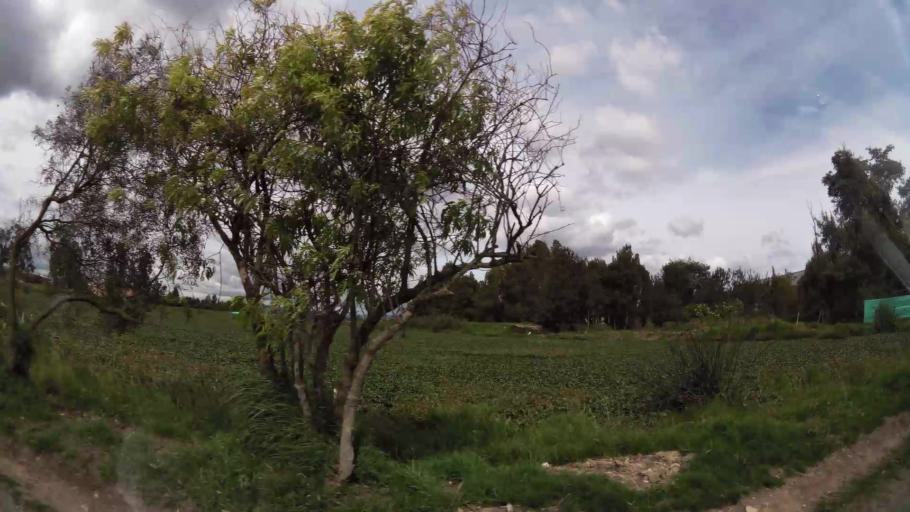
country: CO
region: Cundinamarca
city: Funza
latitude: 4.7012
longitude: -74.2014
